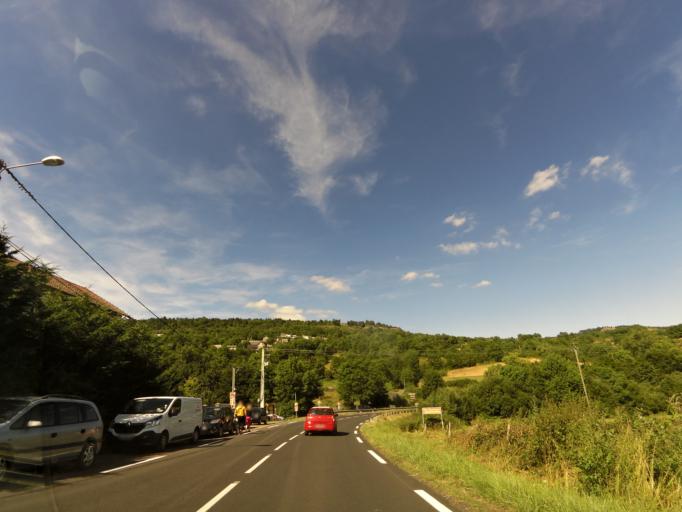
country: FR
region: Auvergne
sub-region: Departement du Puy-de-Dome
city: Aydat
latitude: 45.5888
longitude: 2.9626
